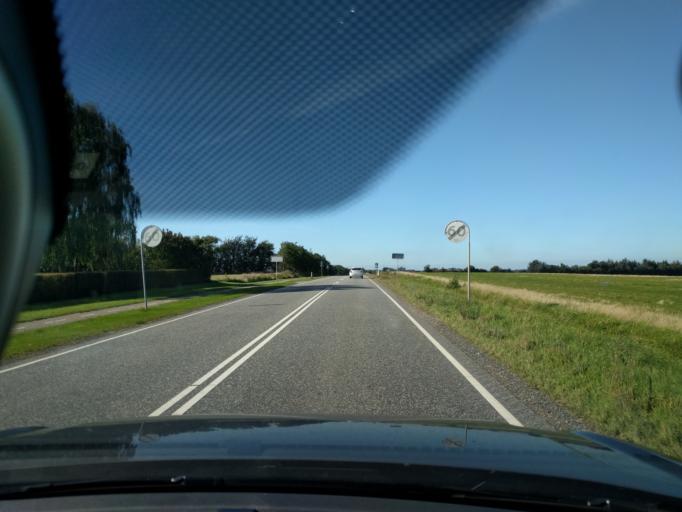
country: DK
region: North Denmark
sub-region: Mariagerfjord Kommune
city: Hobro
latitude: 56.6761
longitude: 9.6732
